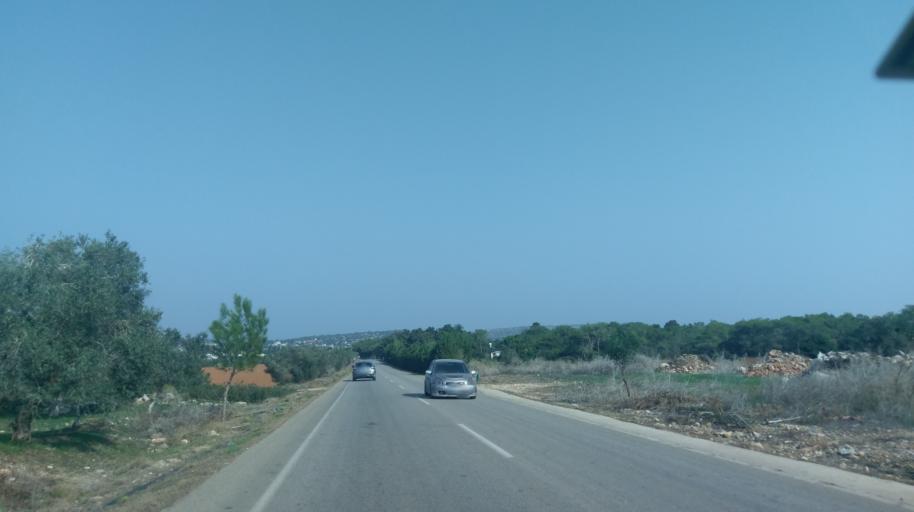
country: CY
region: Ammochostos
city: Leonarisso
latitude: 35.4905
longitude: 34.1539
